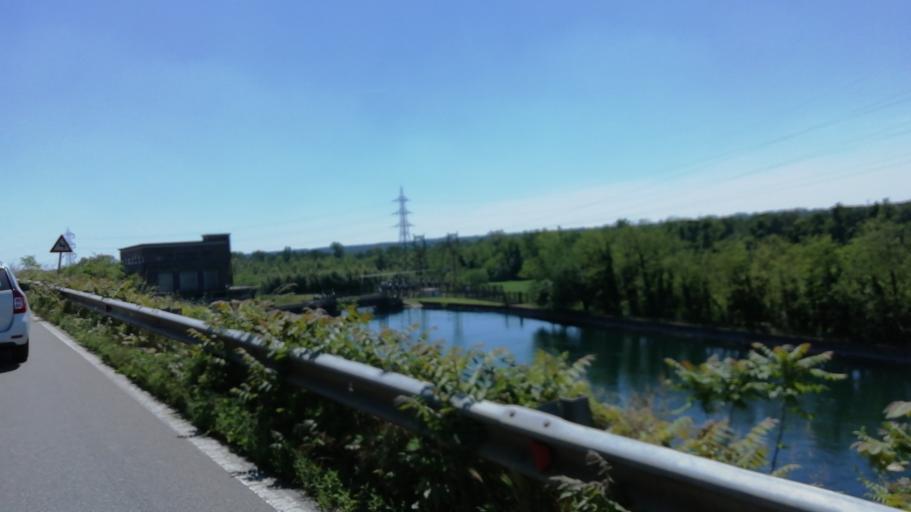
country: IT
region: Lombardy
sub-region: Citta metropolitana di Milano
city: Nosate
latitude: 45.5841
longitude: 8.7073
